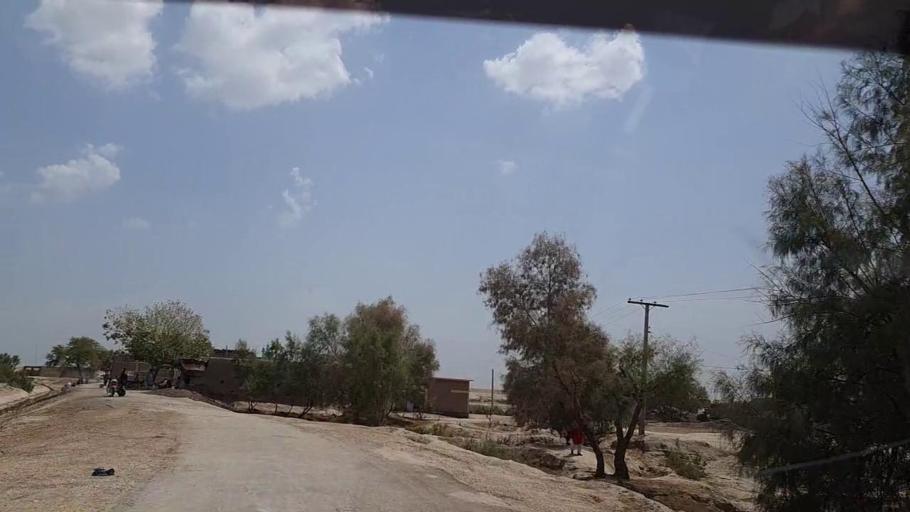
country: PK
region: Sindh
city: Bhan
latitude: 26.5054
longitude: 67.6393
